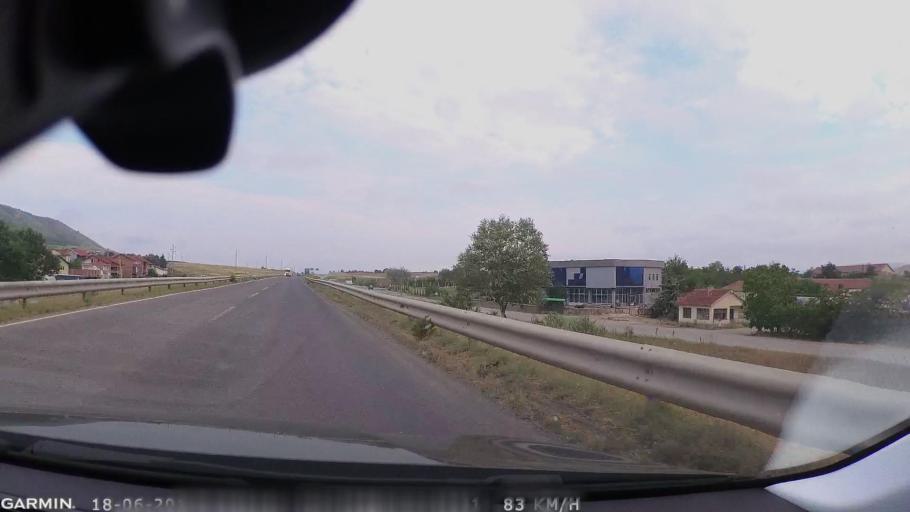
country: MK
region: Stip
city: Shtip
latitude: 41.7754
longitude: 22.1364
